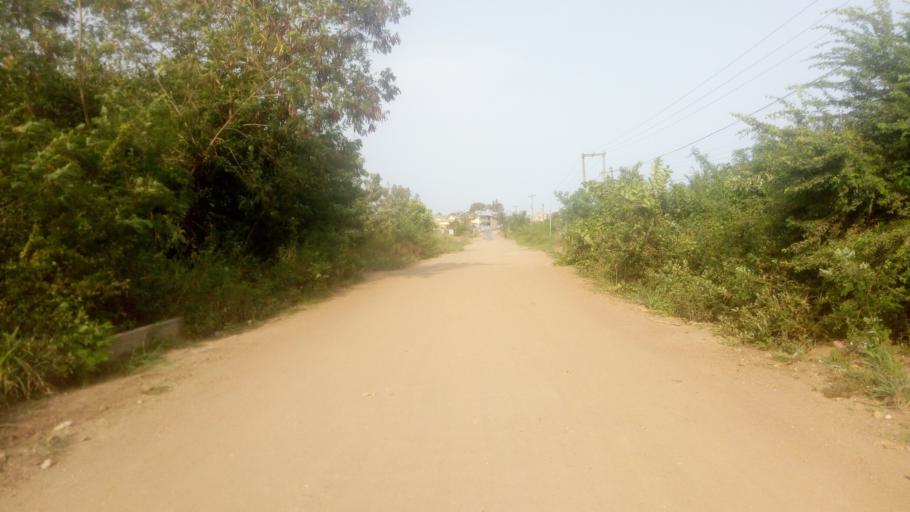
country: GH
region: Central
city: Winneba
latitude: 5.3767
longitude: -0.6369
